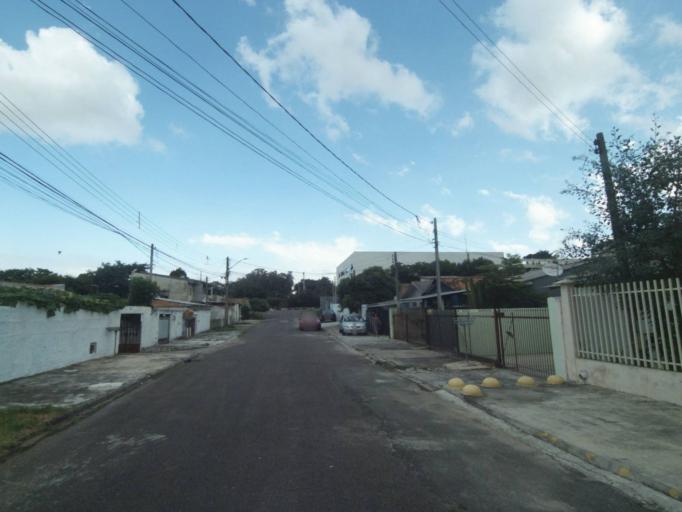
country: BR
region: Parana
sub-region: Pinhais
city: Pinhais
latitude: -25.4466
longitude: -49.2139
